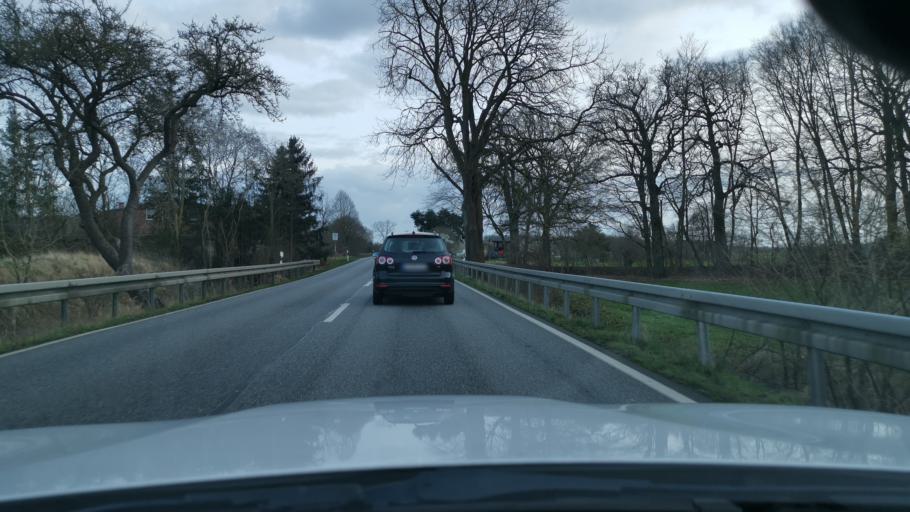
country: DE
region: Mecklenburg-Vorpommern
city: Dummerstorf
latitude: 53.9964
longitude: 12.2647
